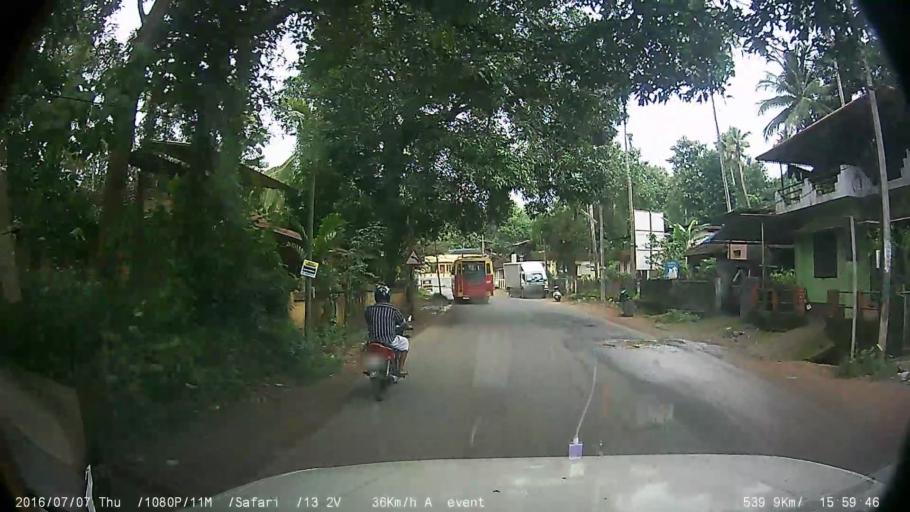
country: IN
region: Kerala
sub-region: Ernakulam
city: Piravam
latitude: 9.8558
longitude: 76.5965
